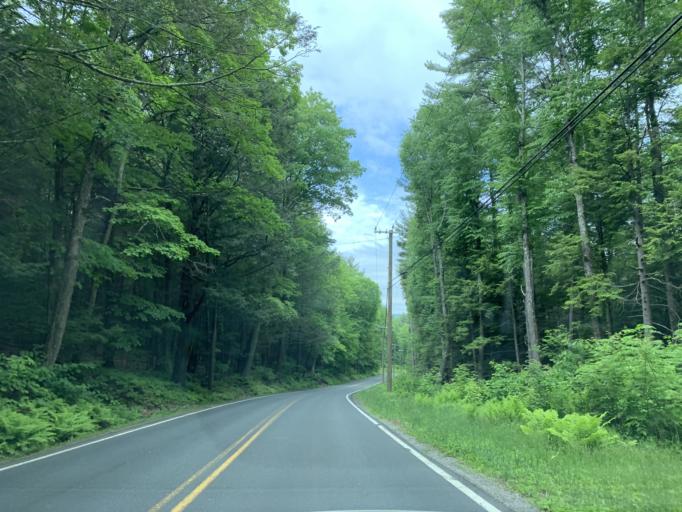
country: US
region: Massachusetts
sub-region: Hampshire County
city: Westhampton
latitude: 42.2355
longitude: -72.8384
